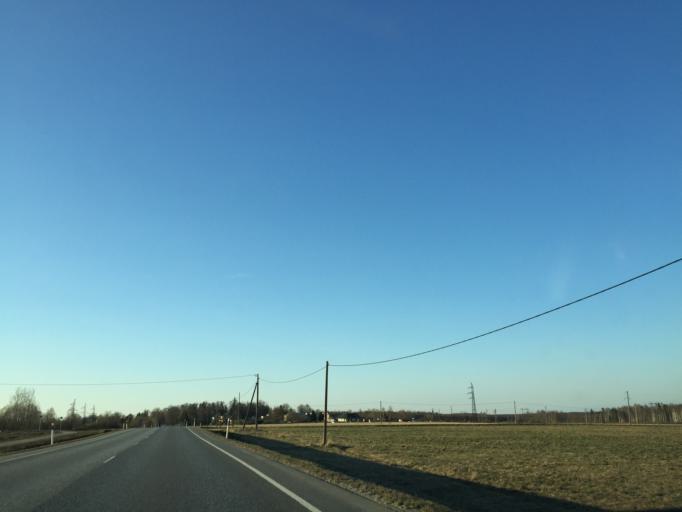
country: EE
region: Ida-Virumaa
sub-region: Johvi vald
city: Johvi
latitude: 59.2646
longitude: 27.5145
